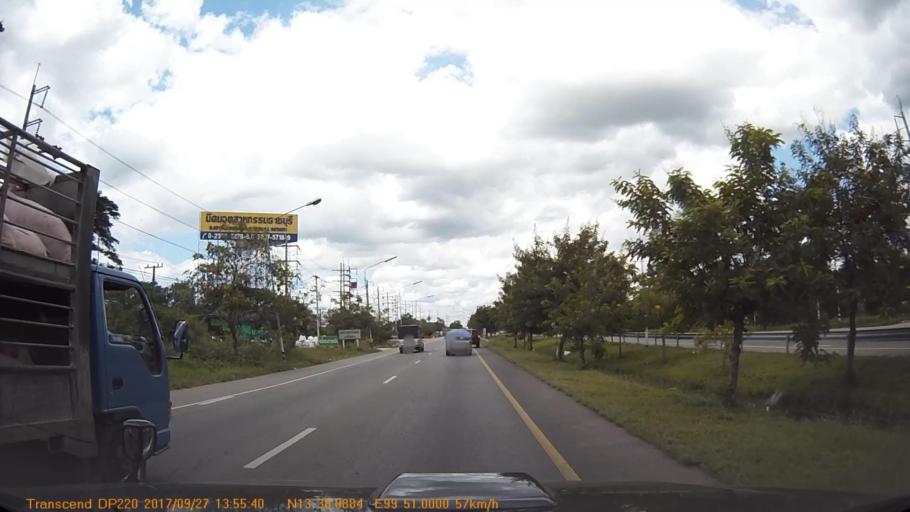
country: TH
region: Ratchaburi
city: Photharam
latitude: 13.6348
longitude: 99.8500
